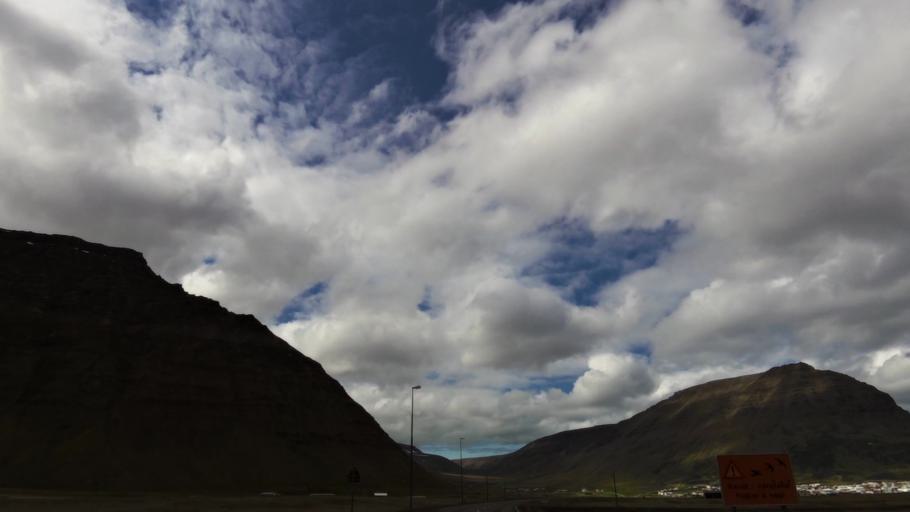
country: IS
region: Westfjords
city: Isafjoerdur
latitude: 66.1448
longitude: -23.2333
